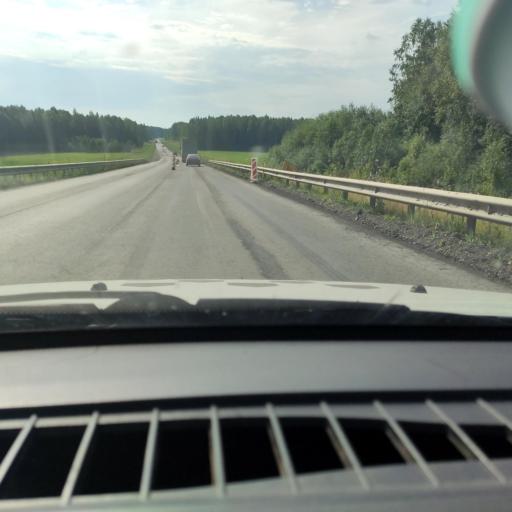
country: RU
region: Perm
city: Siva
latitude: 58.4570
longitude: 54.4113
